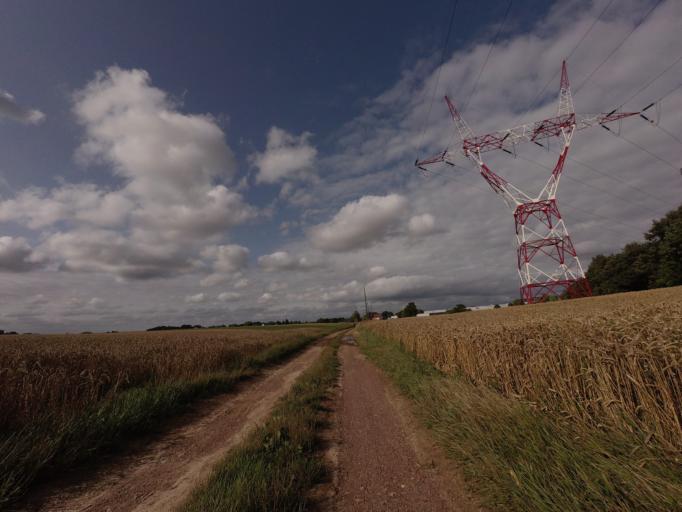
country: BE
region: Flanders
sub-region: Provincie Vlaams-Brabant
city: Vilvoorde
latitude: 50.9368
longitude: 4.4015
